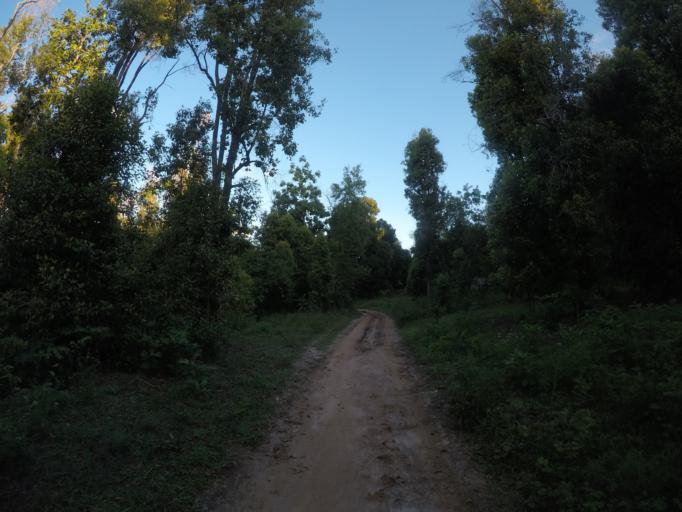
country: TZ
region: Pemba South
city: Mtambile
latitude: -5.3800
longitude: 39.7114
